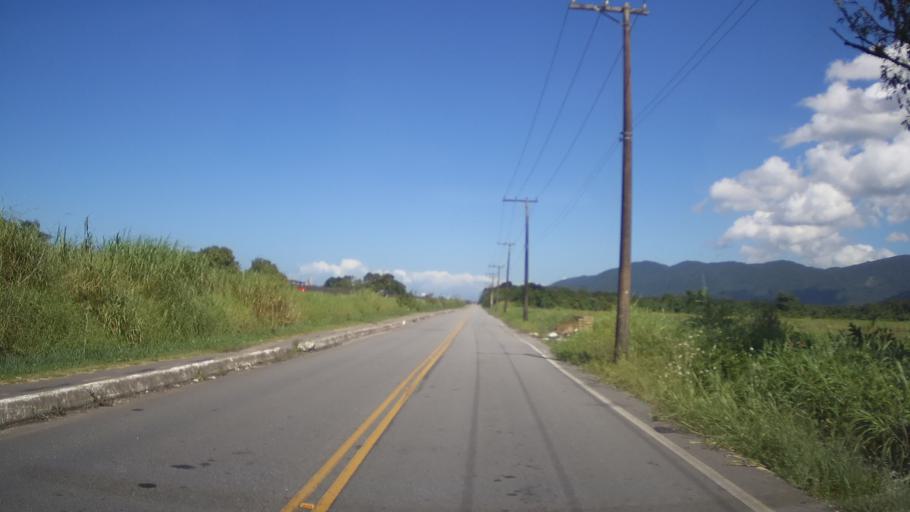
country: BR
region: Sao Paulo
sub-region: Mongagua
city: Mongagua
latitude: -24.0453
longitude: -46.5326
